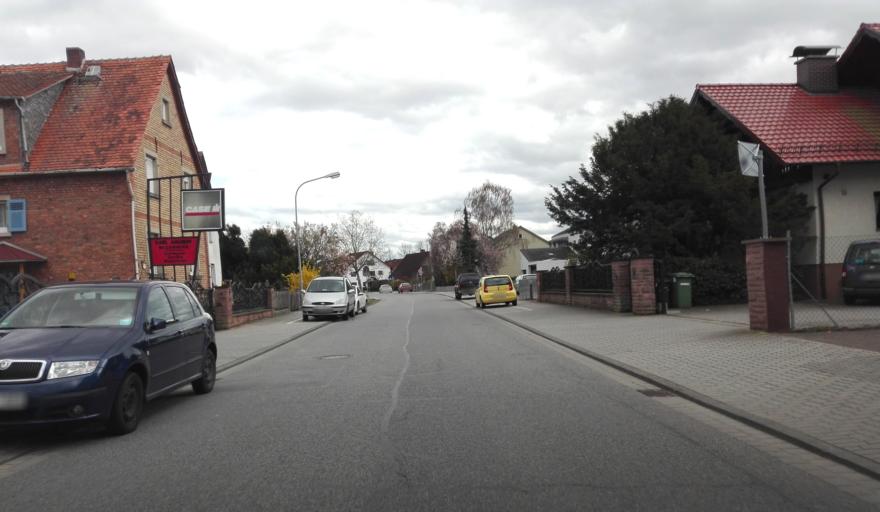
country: DE
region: Hesse
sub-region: Regierungsbezirk Darmstadt
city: Einhausen
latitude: 49.6964
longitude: 8.5698
